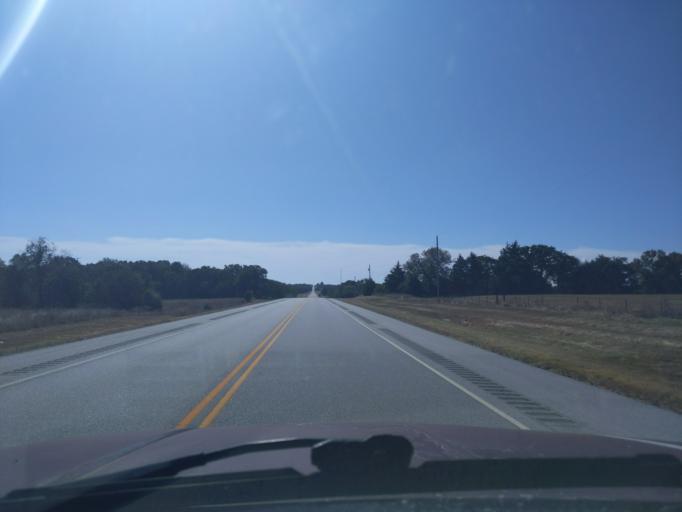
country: US
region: Oklahoma
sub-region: Creek County
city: Bristow
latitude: 35.7459
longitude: -96.3872
